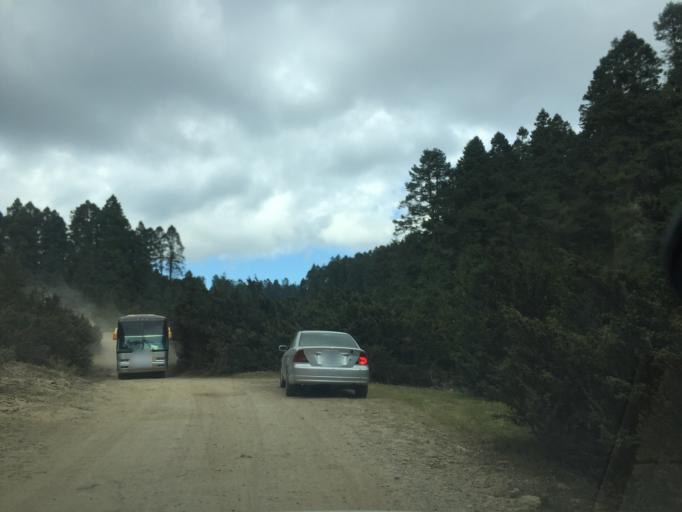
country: MX
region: Michoacan
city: Mineral de Angangueo
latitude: 19.6651
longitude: -100.2736
